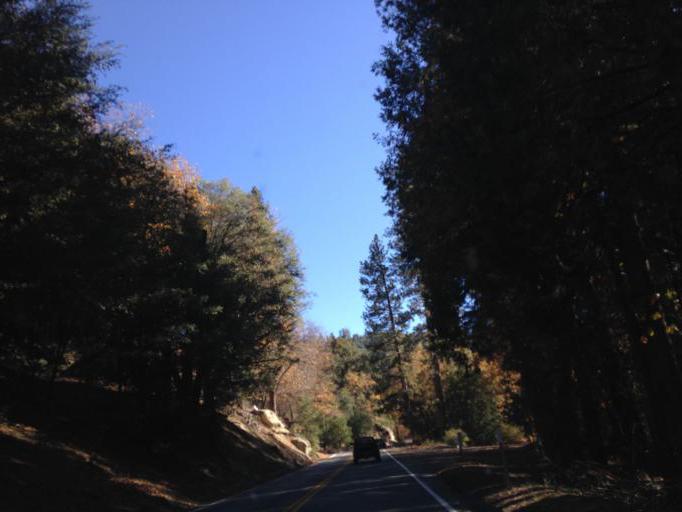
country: US
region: California
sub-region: Riverside County
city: Idyllwild-Pine Cove
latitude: 33.7984
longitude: -116.7479
